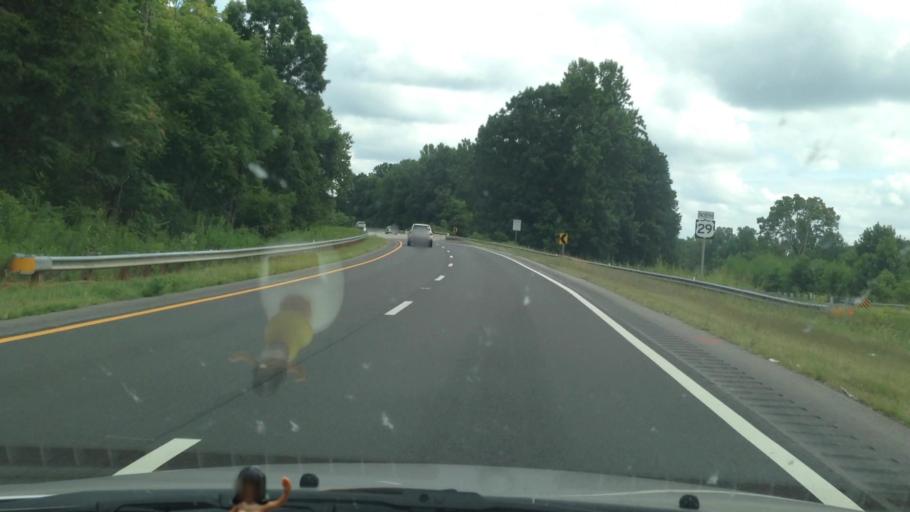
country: US
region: Virginia
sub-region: Pittsylvania County
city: Gretna
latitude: 36.9261
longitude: -79.3756
